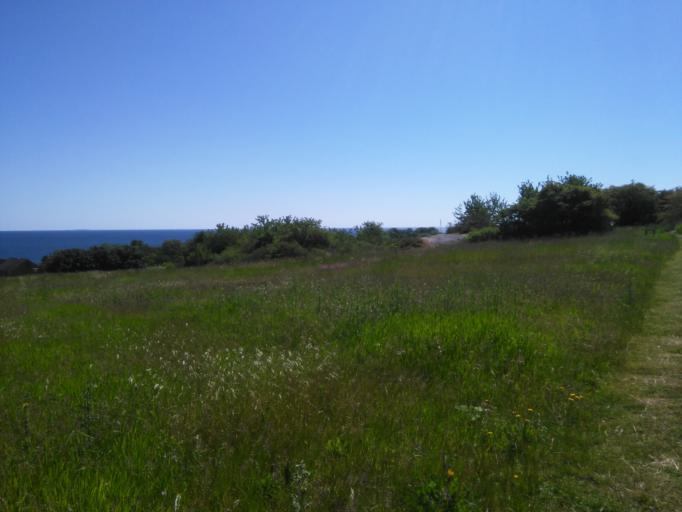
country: DK
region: Capital Region
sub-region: Bornholm Kommune
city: Ronne
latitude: 55.2816
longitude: 14.7889
